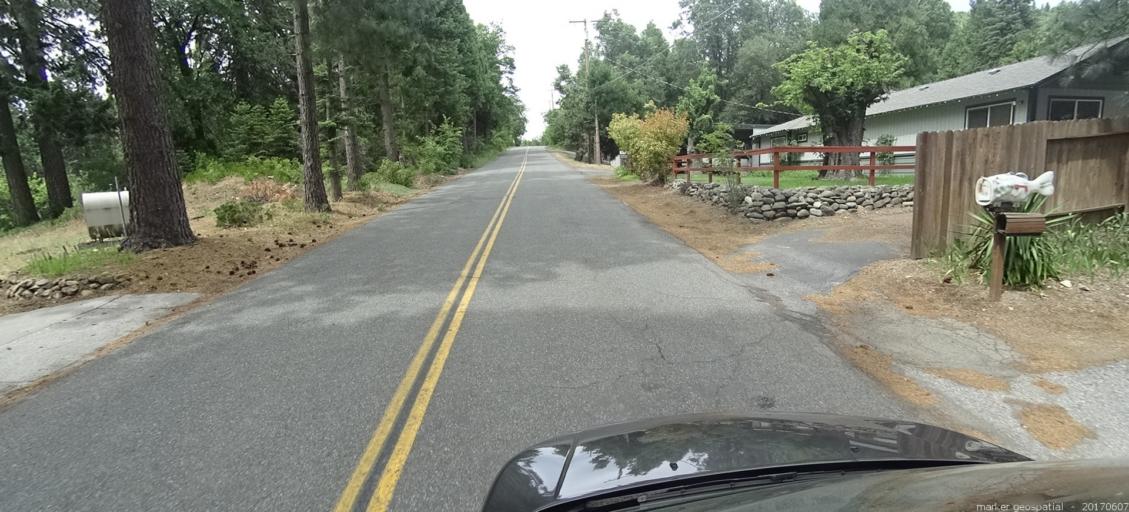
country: US
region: California
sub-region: Siskiyou County
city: Mount Shasta
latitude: 41.3269
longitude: -122.3334
